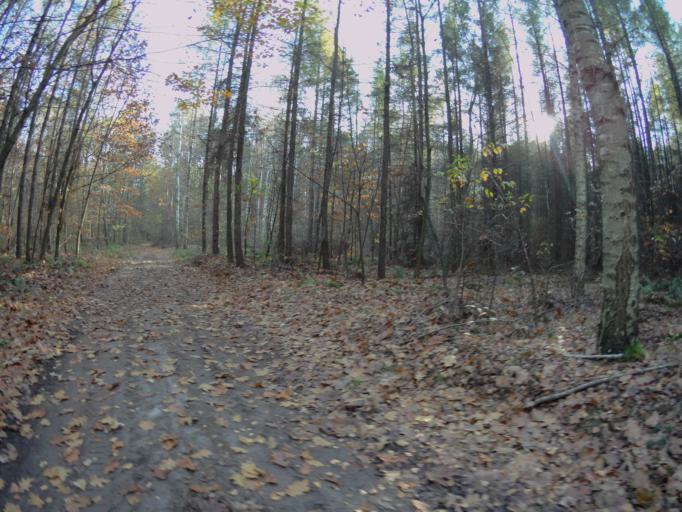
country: PL
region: Subcarpathian Voivodeship
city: Nowa Sarzyna
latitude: 50.3112
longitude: 22.3461
